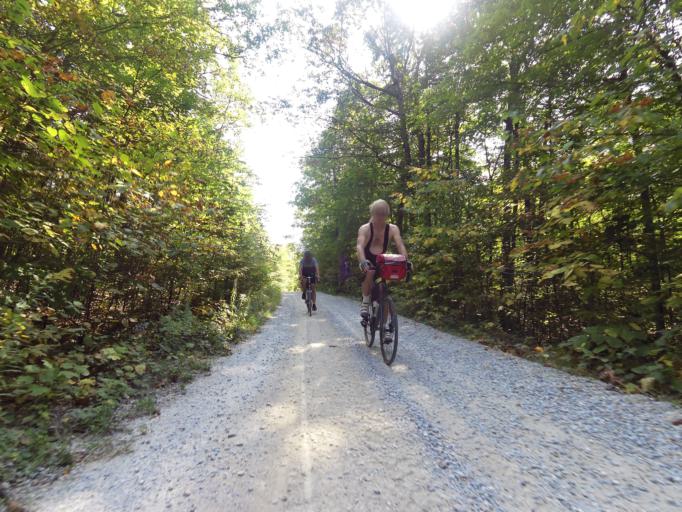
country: CA
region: Ontario
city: Perth
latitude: 45.0198
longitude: -76.6159
